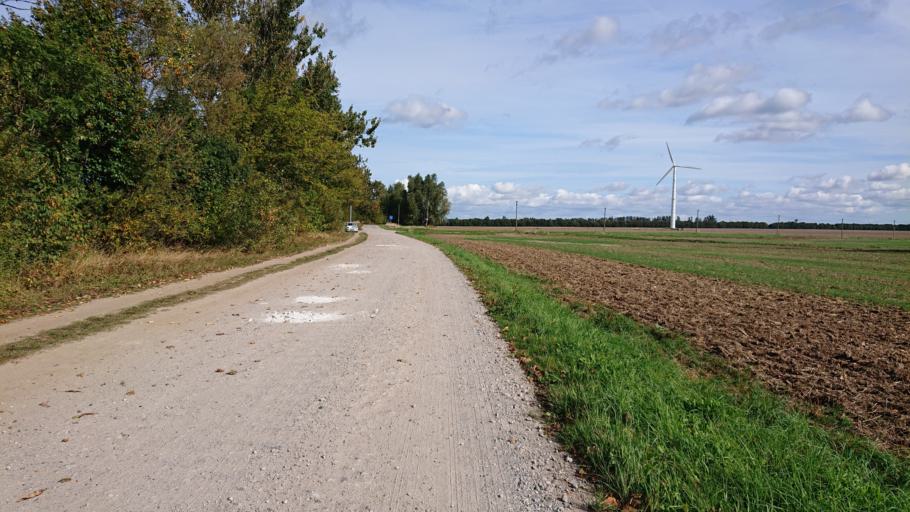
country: DE
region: Mecklenburg-Vorpommern
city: Altefahr
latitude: 54.3448
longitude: 13.1359
